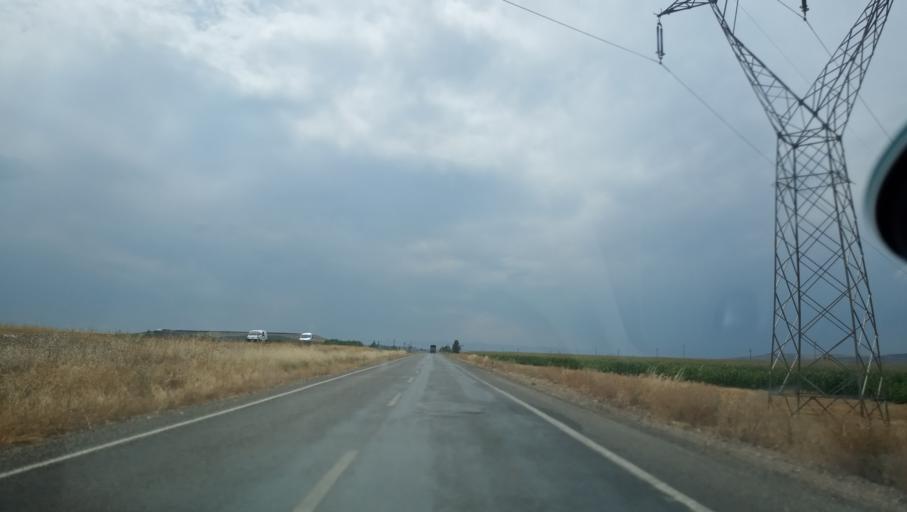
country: TR
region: Diyarbakir
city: Ambar
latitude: 37.8147
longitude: 40.4686
